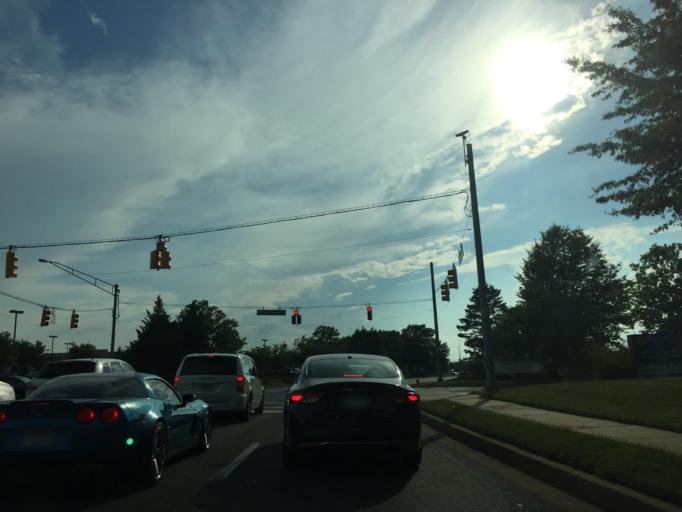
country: US
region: Maryland
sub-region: Baltimore County
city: White Marsh
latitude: 39.3732
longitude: -76.4599
